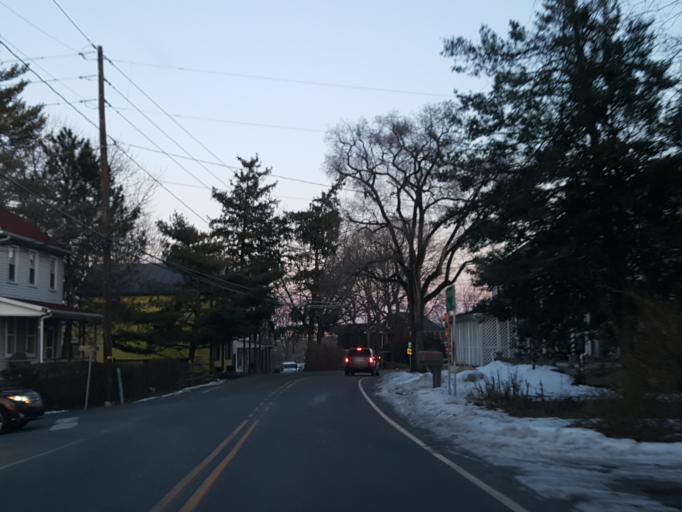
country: US
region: Pennsylvania
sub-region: Dauphin County
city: Hummelstown
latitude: 40.2869
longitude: -76.7247
